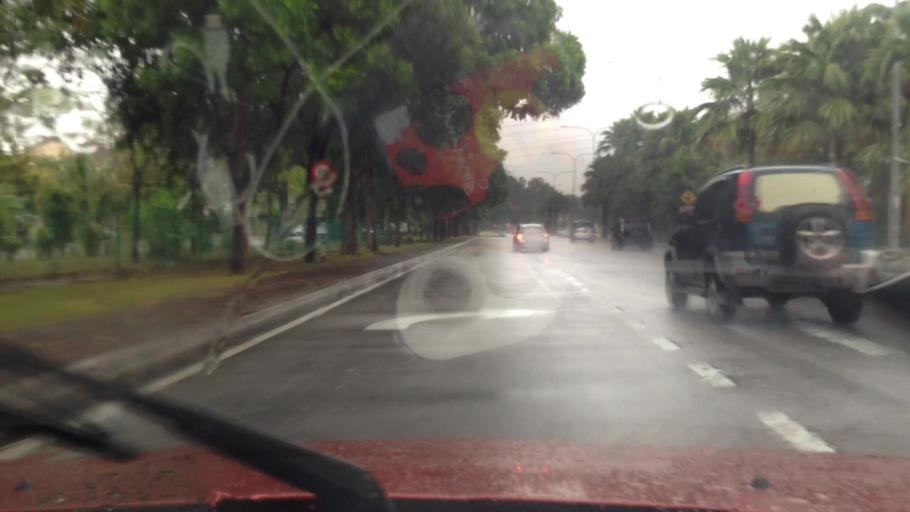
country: MY
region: Selangor
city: Subang Jaya
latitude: 3.0514
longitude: 101.5703
